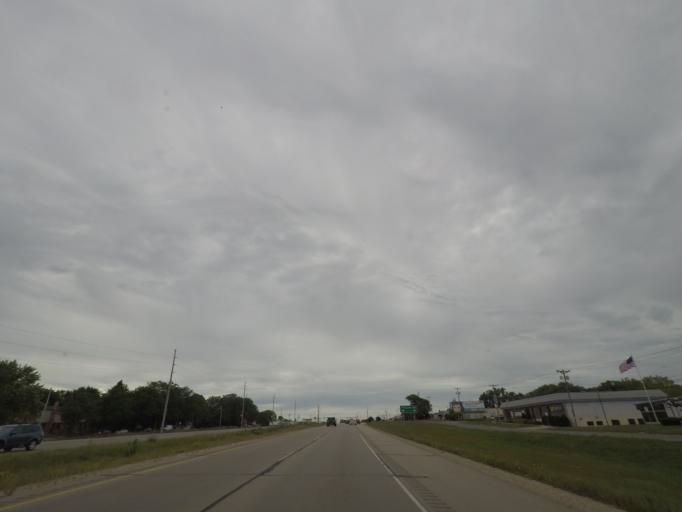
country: US
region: Wisconsin
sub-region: Dane County
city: Monona
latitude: 43.0588
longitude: -89.3092
